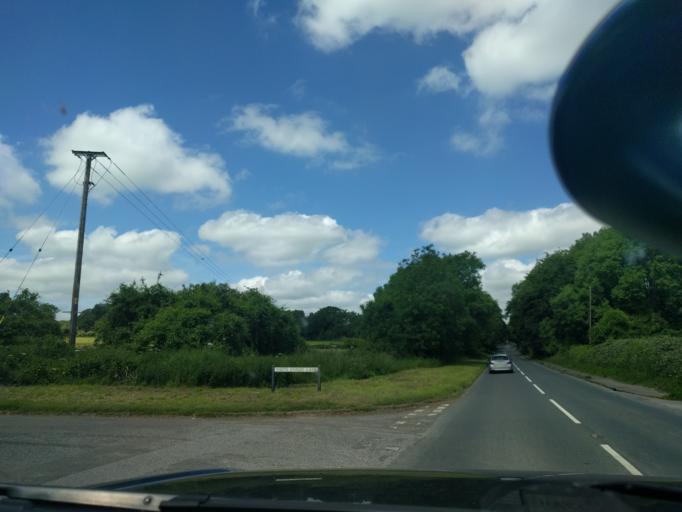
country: GB
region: England
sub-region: Wiltshire
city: Box
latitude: 51.4174
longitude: -2.2281
